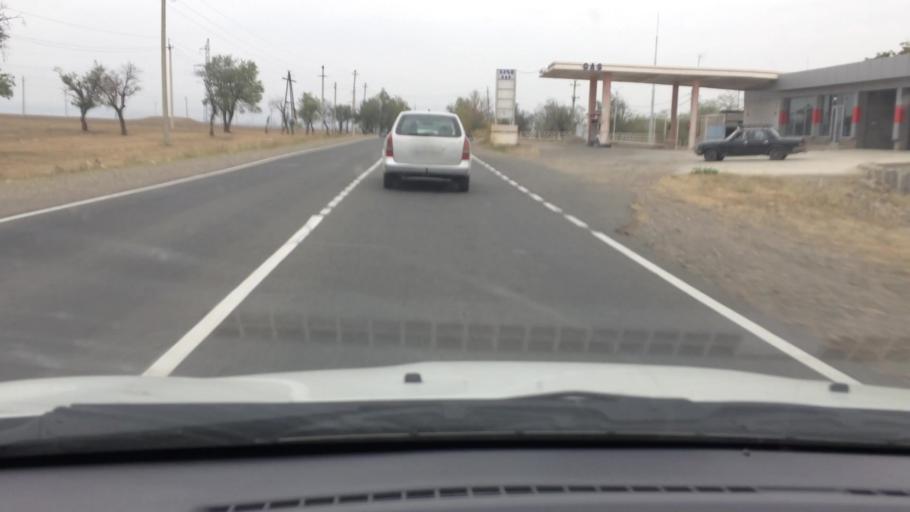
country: GE
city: Naghvarevi
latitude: 41.3819
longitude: 44.8312
